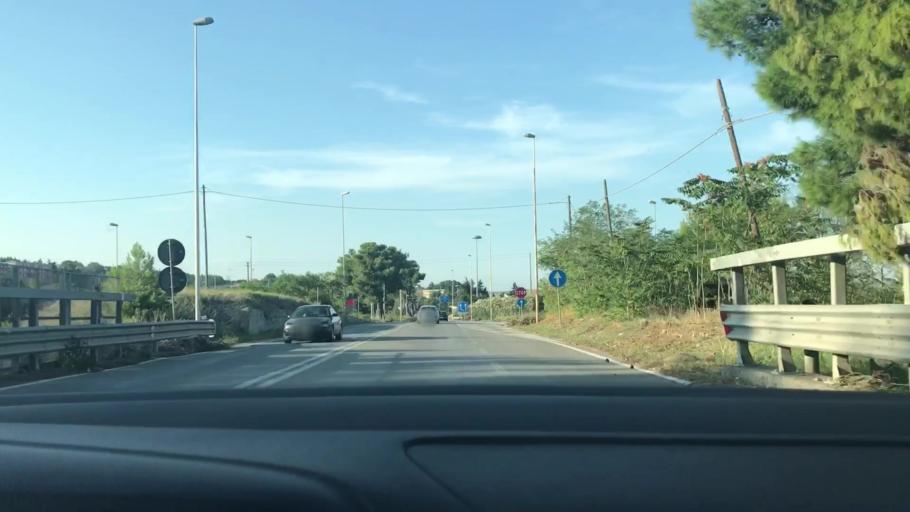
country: IT
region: Basilicate
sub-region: Provincia di Matera
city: Matera
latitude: 40.6845
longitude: 16.5902
